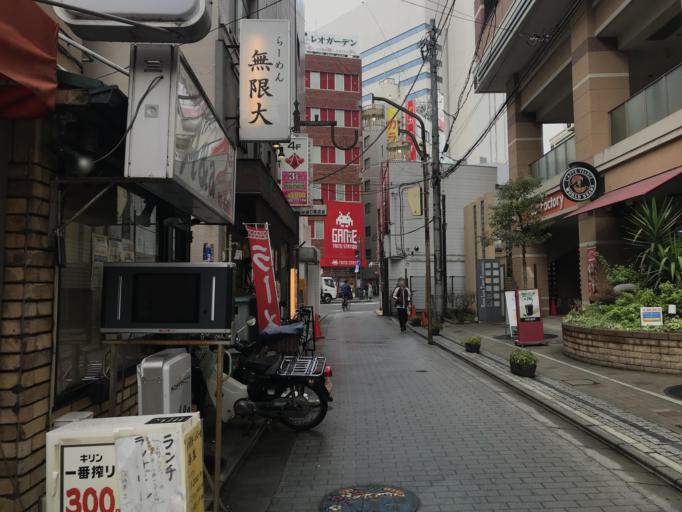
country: JP
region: Chiba
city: Funabashi
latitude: 35.6994
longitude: 139.9866
